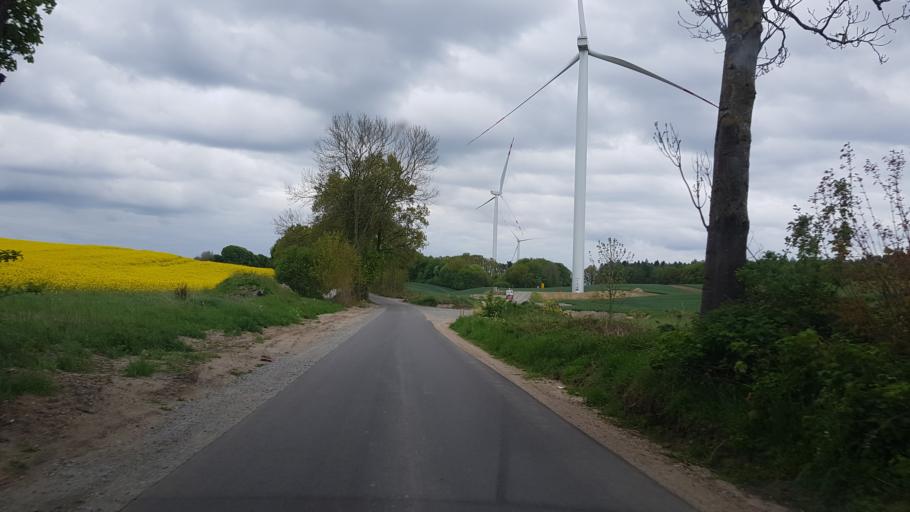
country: PL
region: West Pomeranian Voivodeship
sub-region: Powiat slawienski
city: Slawno
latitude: 54.2652
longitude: 16.5495
